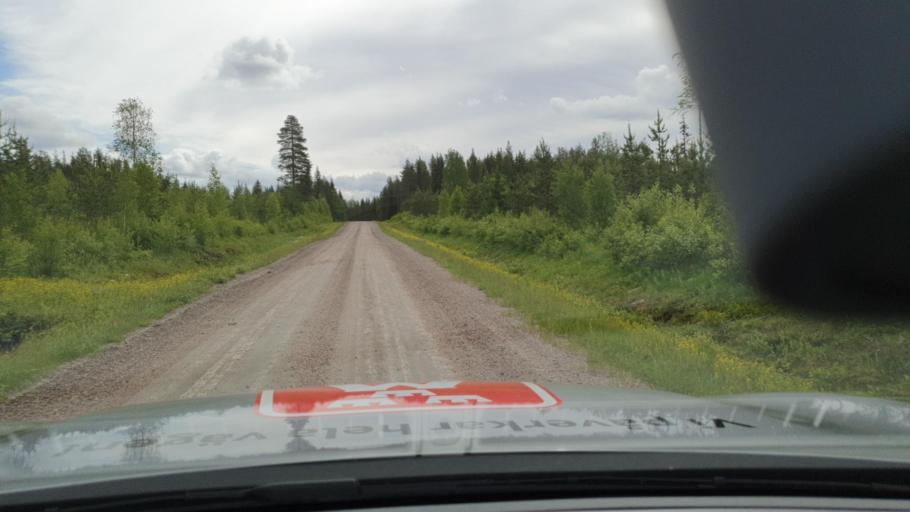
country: SE
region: Norrbotten
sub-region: Kalix Kommun
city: Kalix
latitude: 66.0644
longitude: 23.3147
